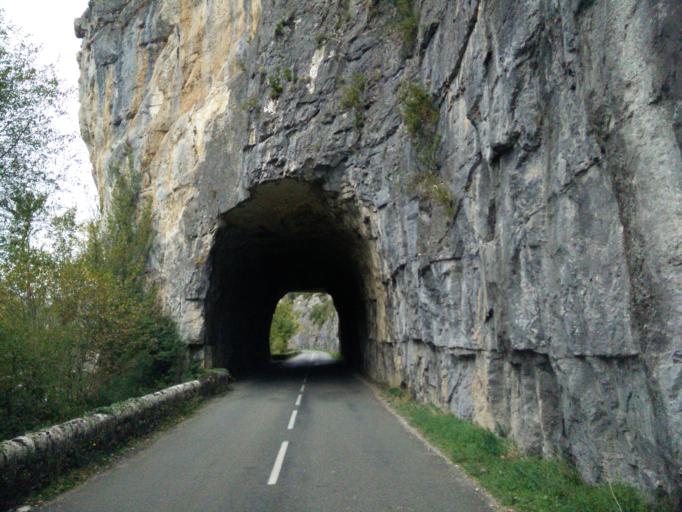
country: FR
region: Midi-Pyrenees
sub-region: Departement du Lot
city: Lalbenque
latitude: 44.4836
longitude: 1.6472
